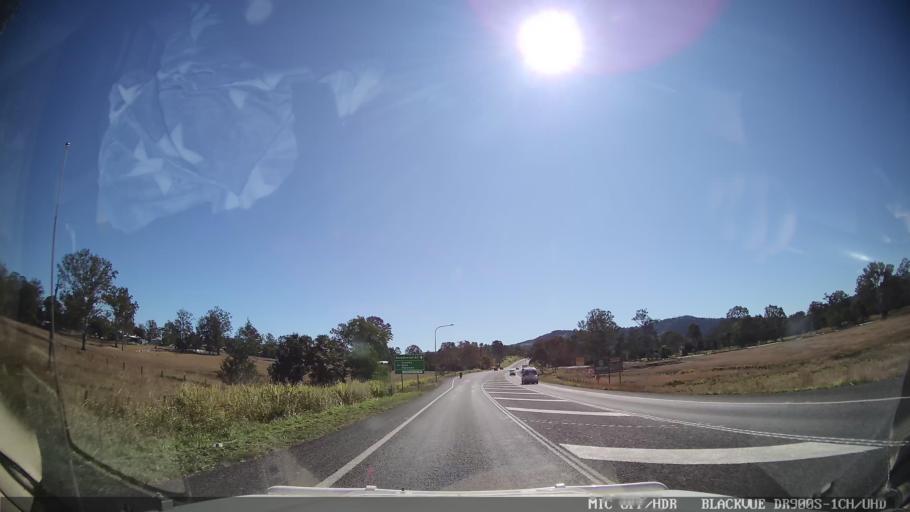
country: AU
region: Queensland
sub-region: Gympie Regional Council
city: Gympie
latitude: -25.9973
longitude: 152.5664
